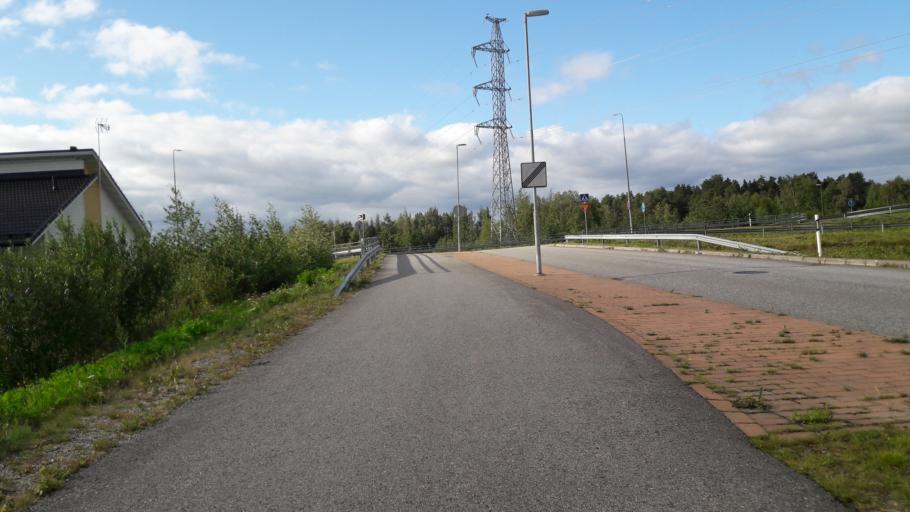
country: FI
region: North Karelia
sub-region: Joensuu
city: Joensuu
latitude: 62.5975
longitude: 29.7935
